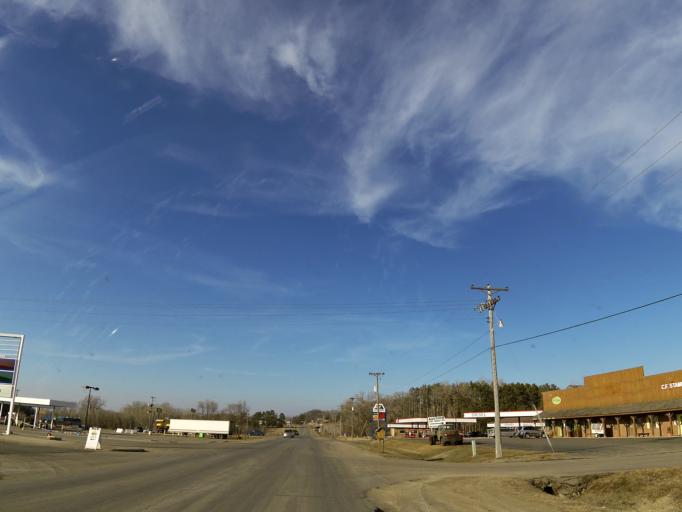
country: US
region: Minnesota
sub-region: Goodhue County
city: Cannon Falls
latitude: 44.4901
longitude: -92.9065
